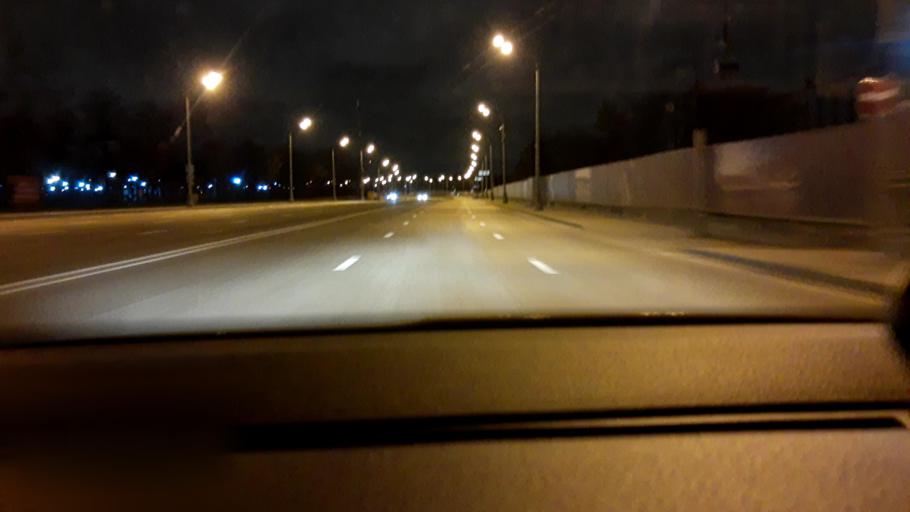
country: RU
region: Moskovskaya
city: Kozhukhovo
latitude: 55.6895
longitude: 37.6739
